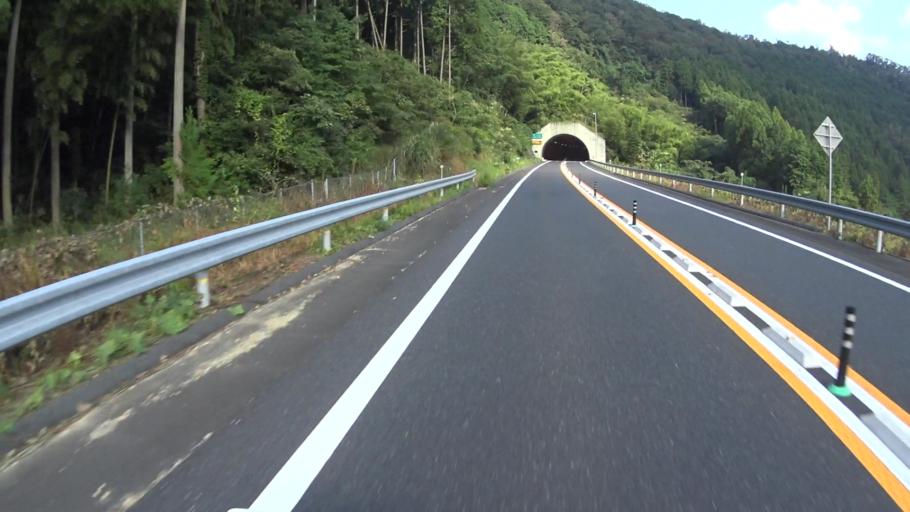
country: JP
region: Kyoto
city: Ayabe
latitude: 35.3142
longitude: 135.3212
